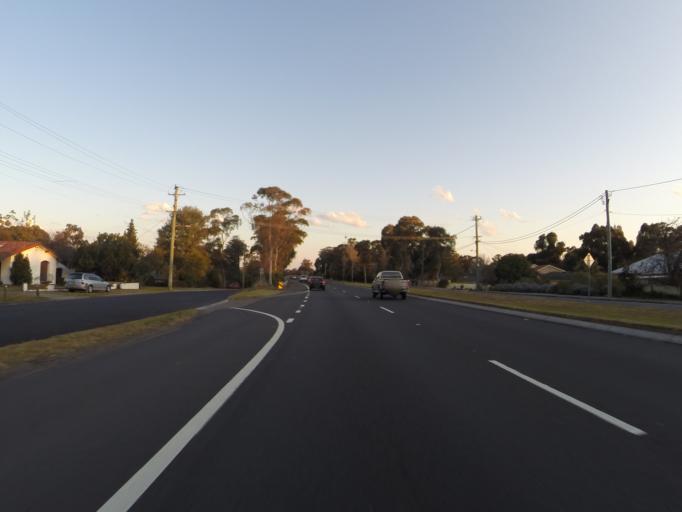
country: AU
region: New South Wales
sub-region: Blue Mountains Municipality
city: Blaxland
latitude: -33.7526
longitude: 150.6115
